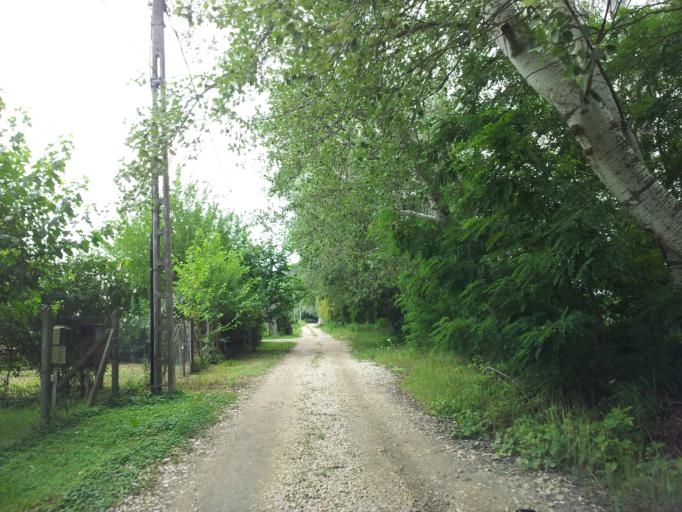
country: HU
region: Pest
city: Szigetcsep
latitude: 47.2224
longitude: 18.9692
